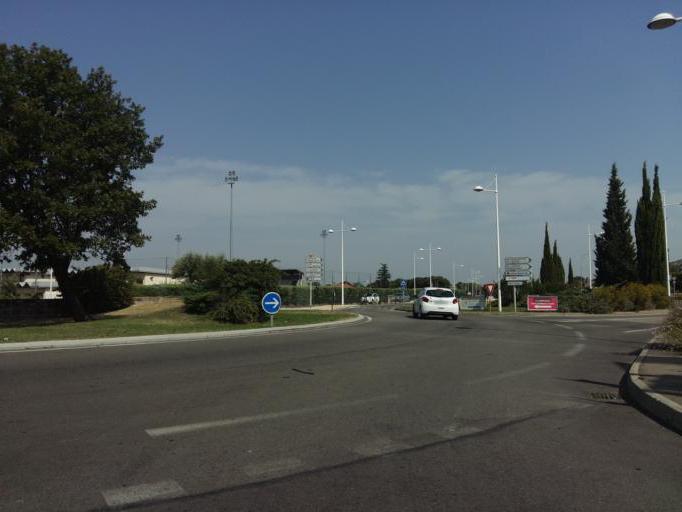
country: FR
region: Provence-Alpes-Cote d'Azur
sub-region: Departement du Vaucluse
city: Bollene
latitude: 44.2932
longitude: 4.7535
